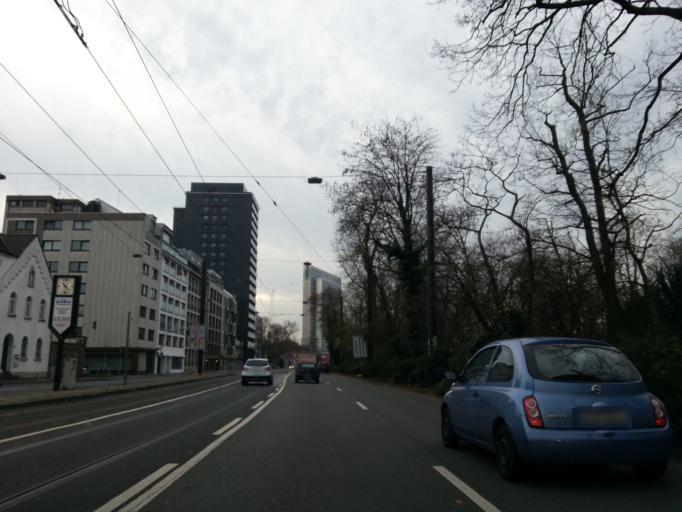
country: DE
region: North Rhine-Westphalia
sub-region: Regierungsbezirk Dusseldorf
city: Dusseldorf
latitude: 51.2327
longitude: 6.7794
